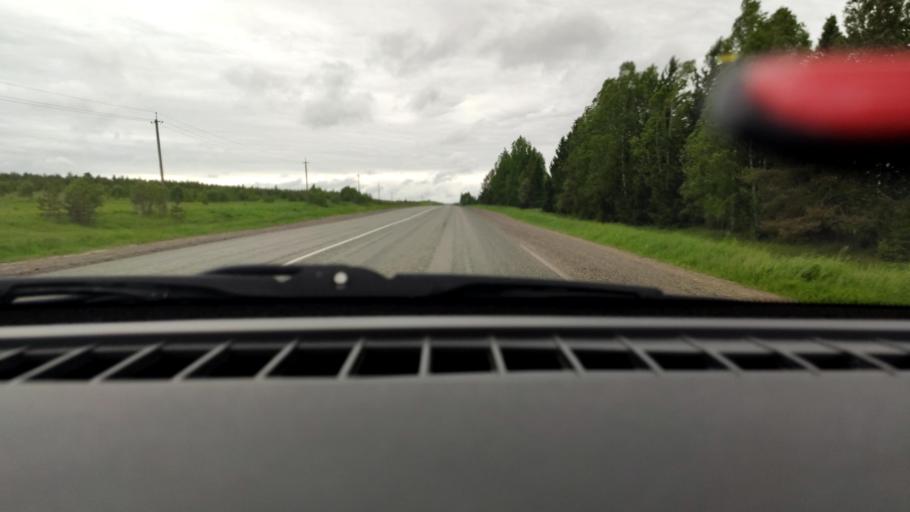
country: RU
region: Perm
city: Mendeleyevo
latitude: 58.0932
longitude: 55.1379
